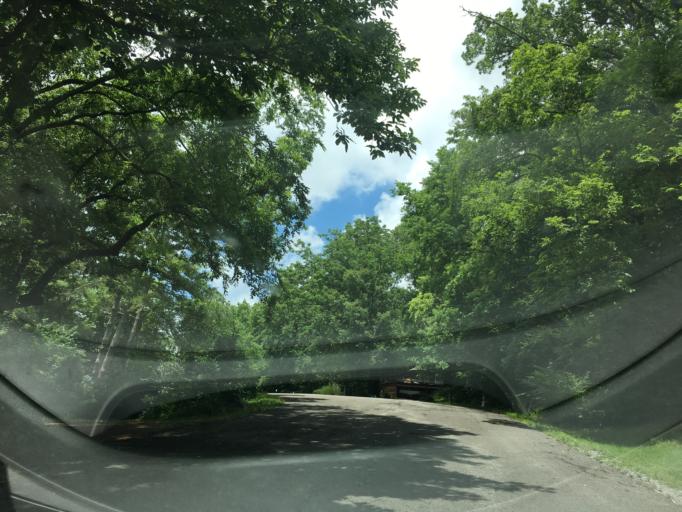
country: US
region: Tennessee
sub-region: Davidson County
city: Forest Hills
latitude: 36.0845
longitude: -86.8453
